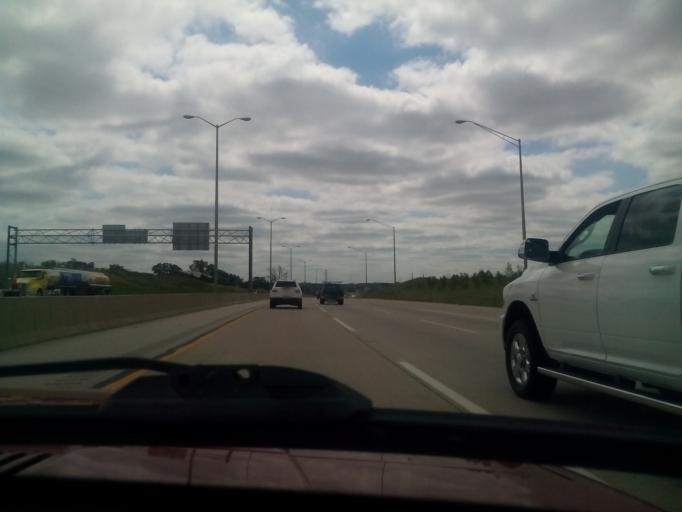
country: US
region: Illinois
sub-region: Cook County
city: Lemont
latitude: 41.6529
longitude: -88.0159
